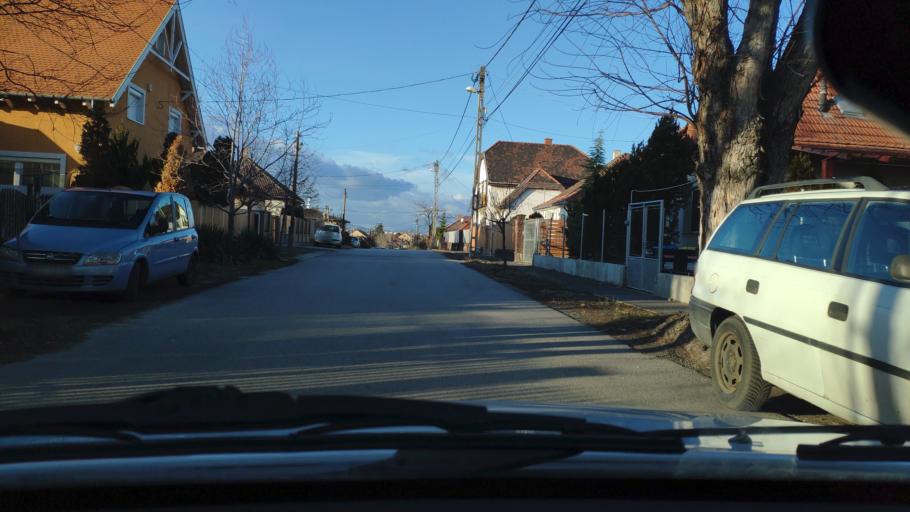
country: HU
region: Budapest
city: Budapest XXIII. keruelet
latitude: 47.3972
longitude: 19.0946
